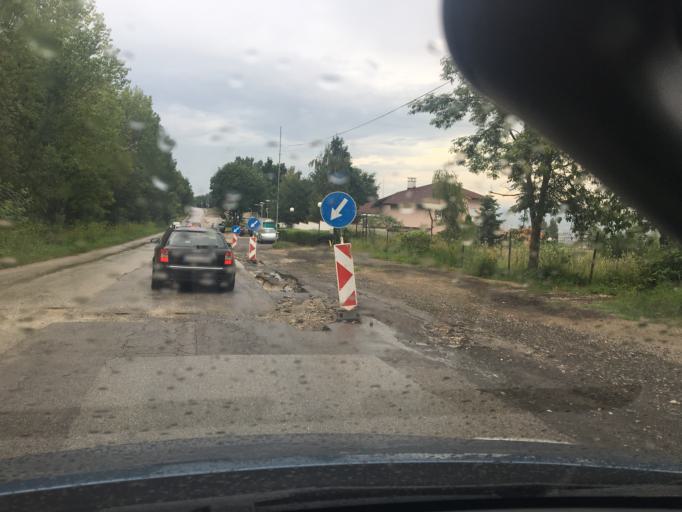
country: BG
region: Sofia-Capital
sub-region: Stolichna Obshtina
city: Sofia
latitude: 42.6387
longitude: 23.2964
